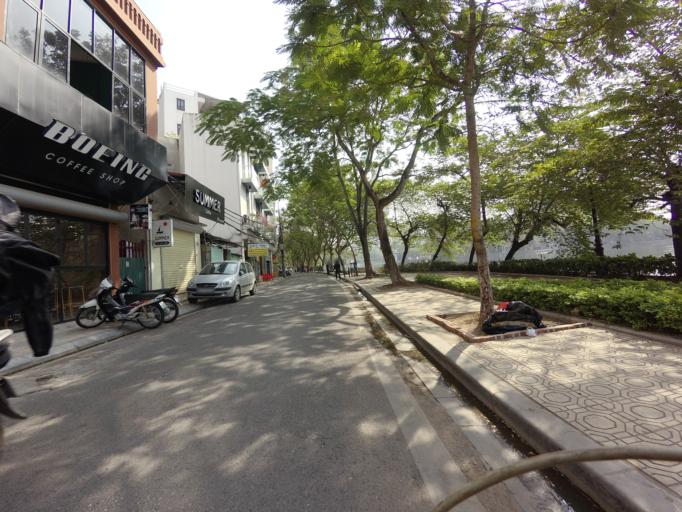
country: VN
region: Ha Noi
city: Hoan Kiem
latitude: 21.0486
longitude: 105.8400
